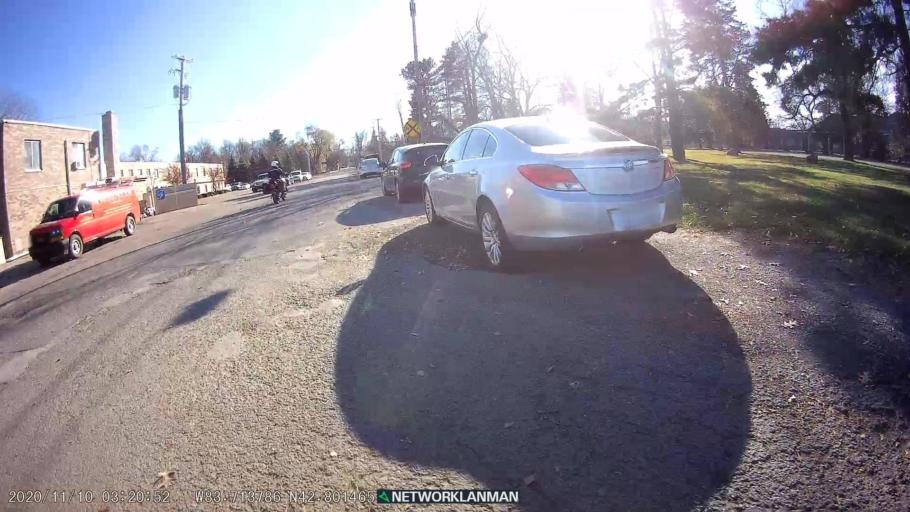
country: US
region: Michigan
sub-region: Genesee County
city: Fenton
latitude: 42.8014
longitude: -83.7137
